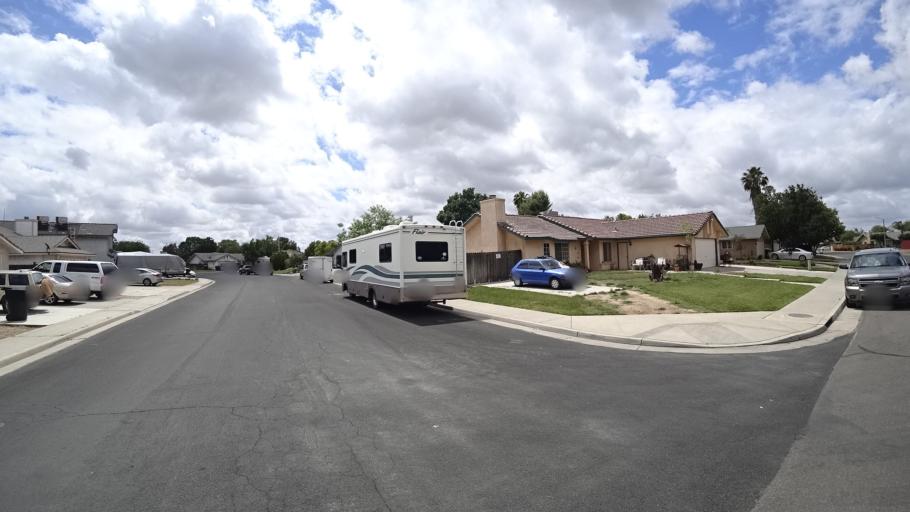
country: US
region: California
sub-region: Kings County
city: Hanford
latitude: 36.3319
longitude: -119.6266
